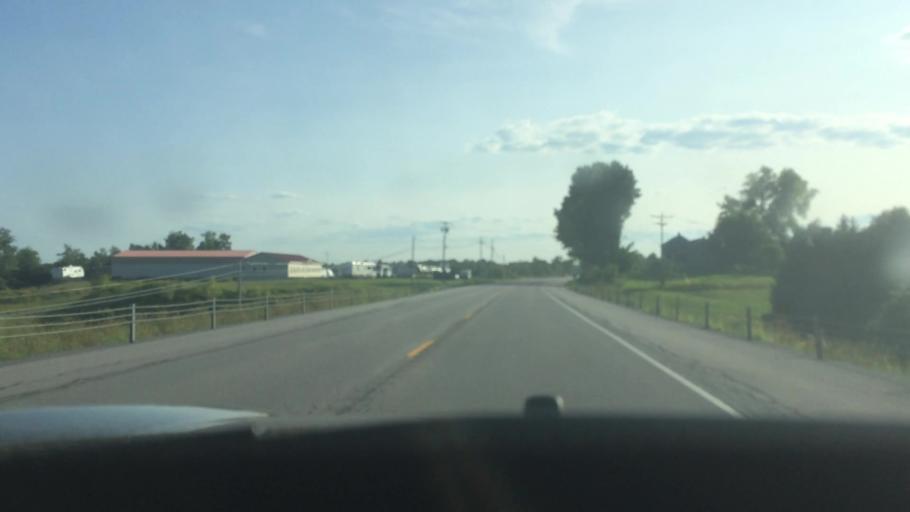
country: US
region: New York
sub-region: St. Lawrence County
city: Potsdam
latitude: 44.6602
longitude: -75.0351
